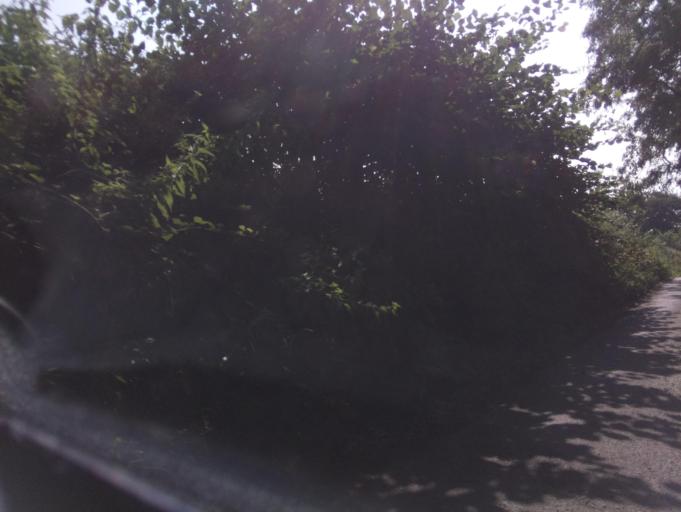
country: GB
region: England
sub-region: Derbyshire
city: Duffield
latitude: 52.9694
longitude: -1.5163
